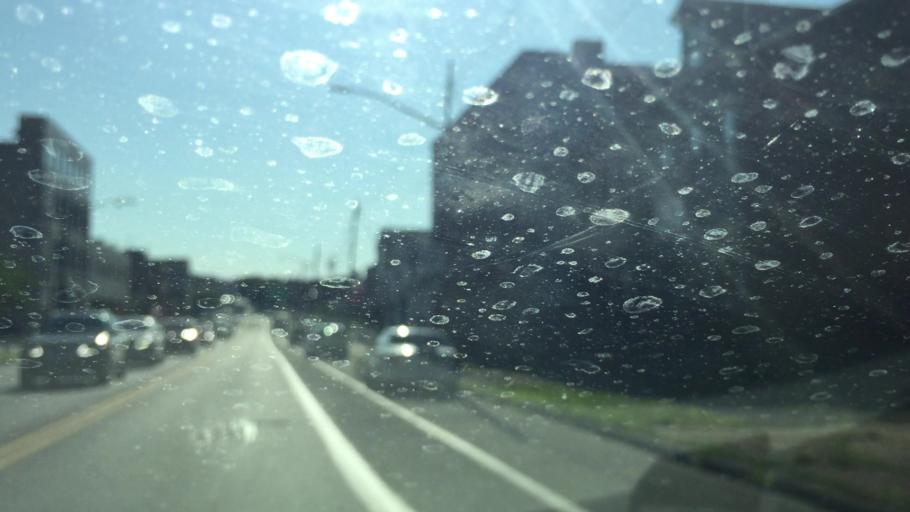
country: US
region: Pennsylvania
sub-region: Allegheny County
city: Bloomfield
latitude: 40.4629
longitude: -79.9566
